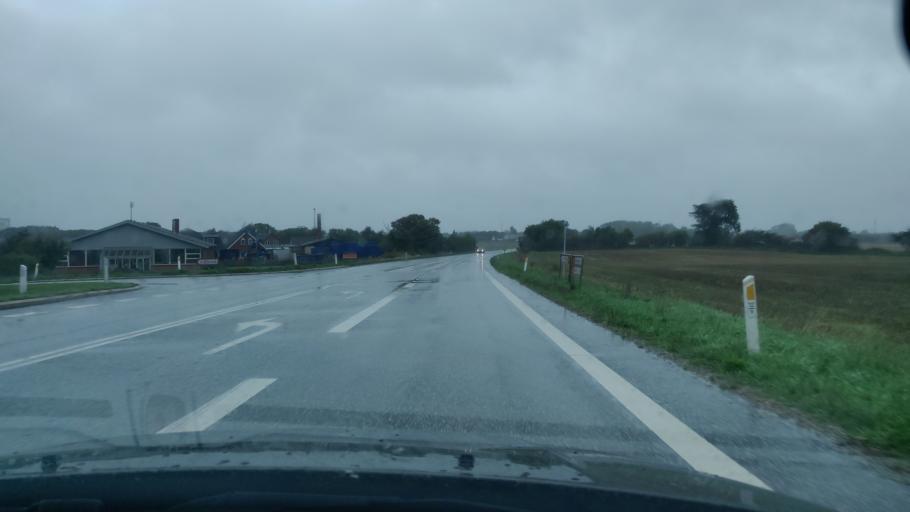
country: DK
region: North Denmark
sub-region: Thisted Kommune
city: Thisted
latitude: 56.8675
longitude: 8.5715
